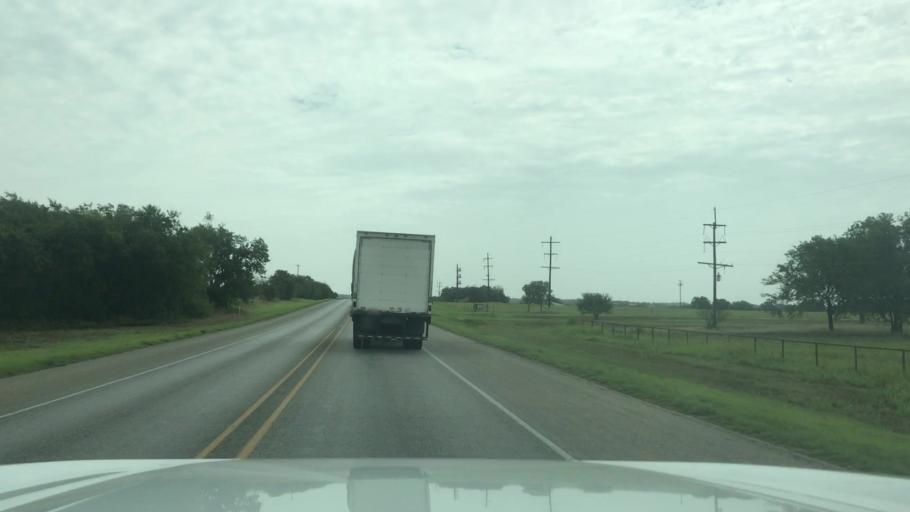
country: US
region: Texas
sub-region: Comanche County
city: De Leon
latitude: 32.0976
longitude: -98.4641
